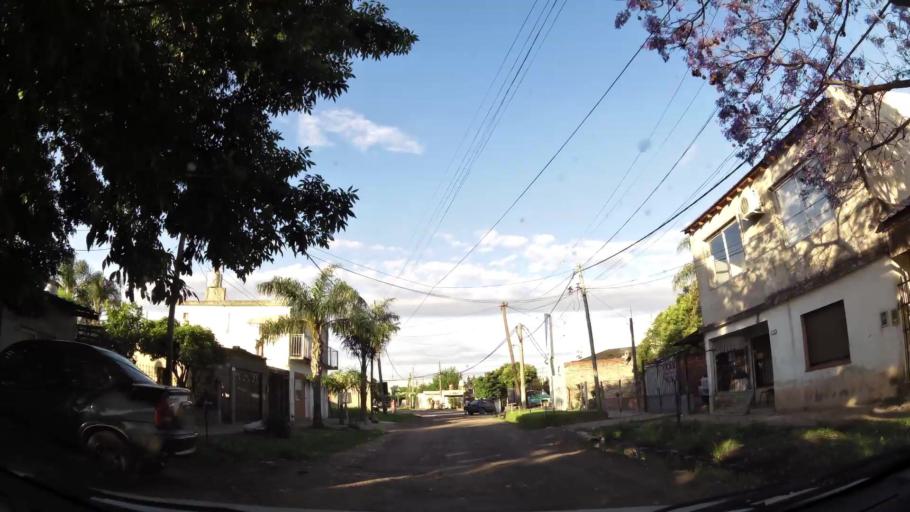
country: AR
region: Buenos Aires
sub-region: Partido de Merlo
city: Merlo
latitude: -34.6980
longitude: -58.7522
